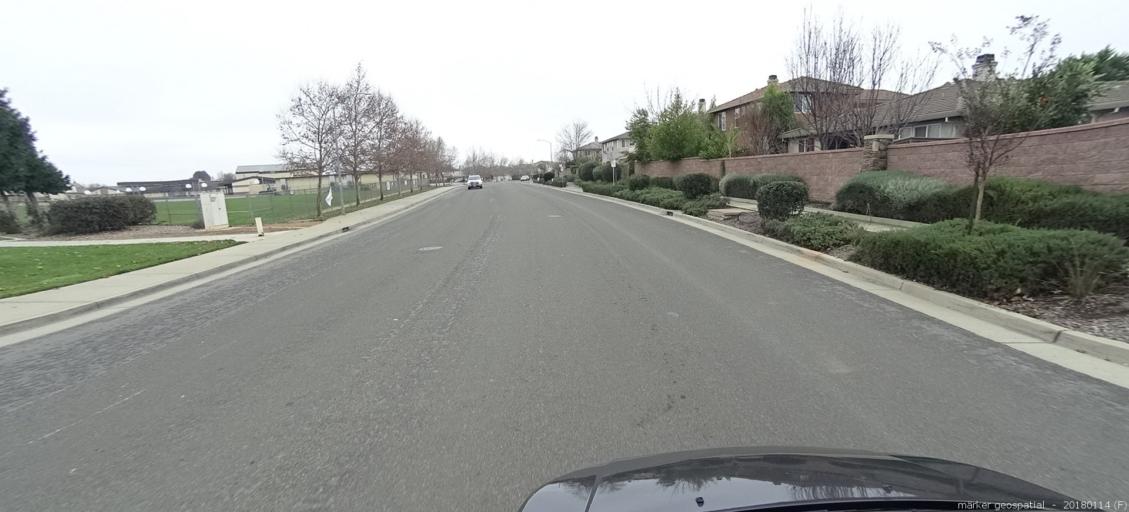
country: US
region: California
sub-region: Sacramento County
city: Gold River
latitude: 38.5566
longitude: -121.2395
